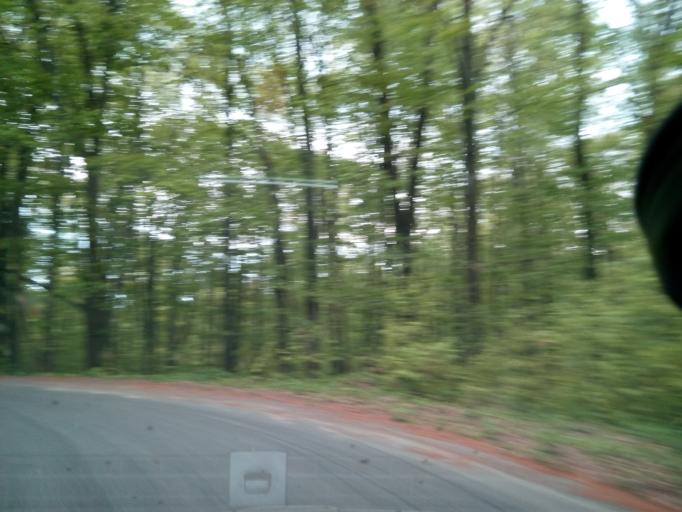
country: SK
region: Kosicky
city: Secovce
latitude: 48.8123
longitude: 21.5237
